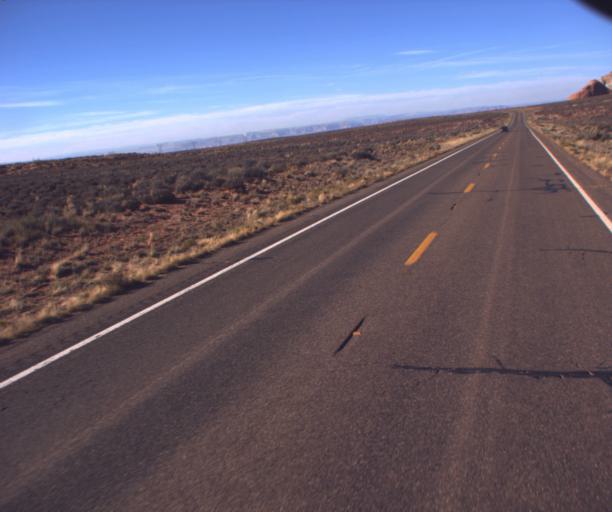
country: US
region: Arizona
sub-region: Coconino County
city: LeChee
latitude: 36.8207
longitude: -111.3078
